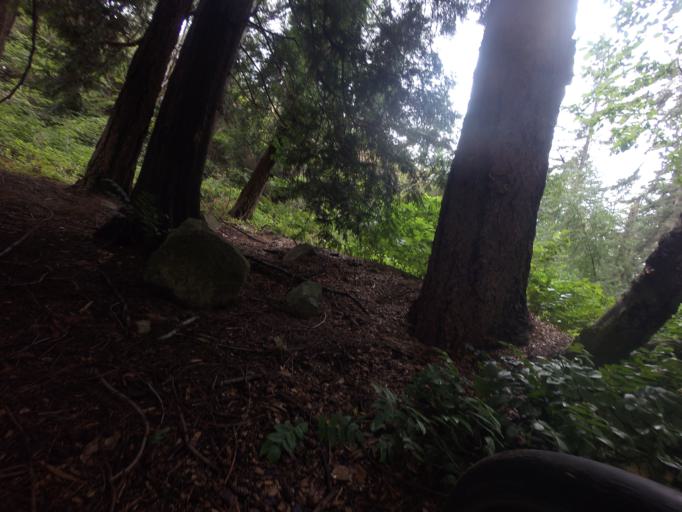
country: CA
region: British Columbia
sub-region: Greater Vancouver Regional District
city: Bowen Island
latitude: 49.3320
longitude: -123.2638
